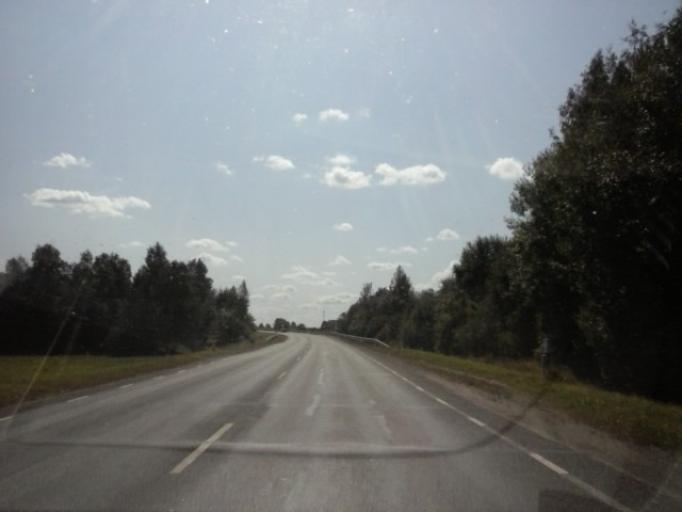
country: EE
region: Tartu
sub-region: UElenurme vald
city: Ulenurme
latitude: 58.2830
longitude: 26.7285
